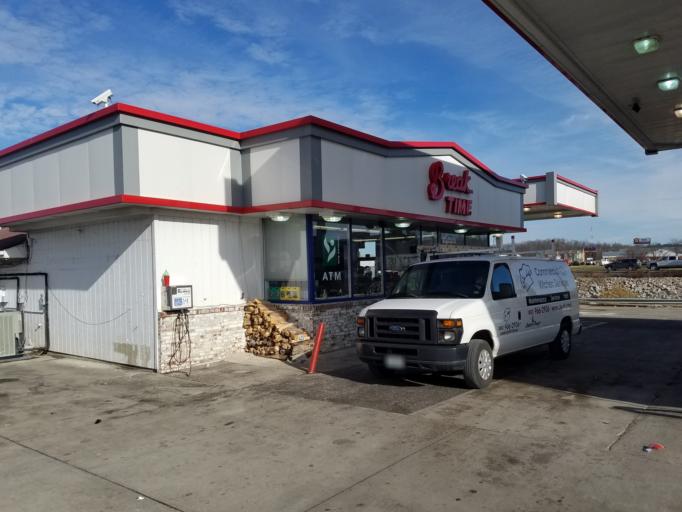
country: US
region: Missouri
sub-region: Boone County
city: Columbia
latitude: 38.9601
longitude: -92.2932
